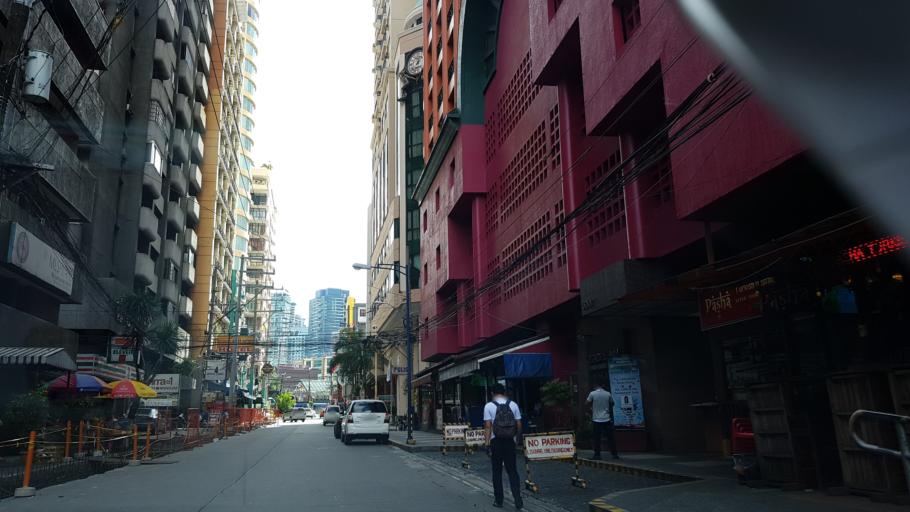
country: PH
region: Metro Manila
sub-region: Makati City
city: Makati City
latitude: 14.5631
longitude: 121.0289
